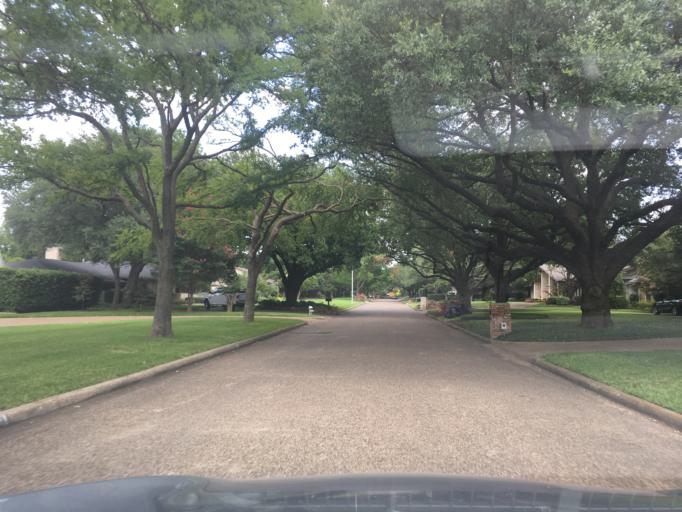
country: US
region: Texas
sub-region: Dallas County
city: University Park
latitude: 32.9009
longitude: -96.8171
